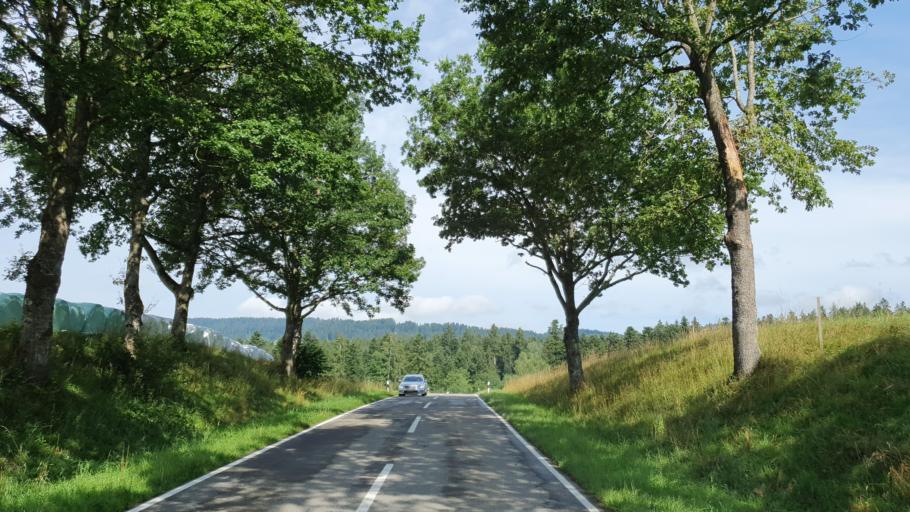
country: DE
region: Bavaria
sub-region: Swabia
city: Scheidegg
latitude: 47.5429
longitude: 9.8645
